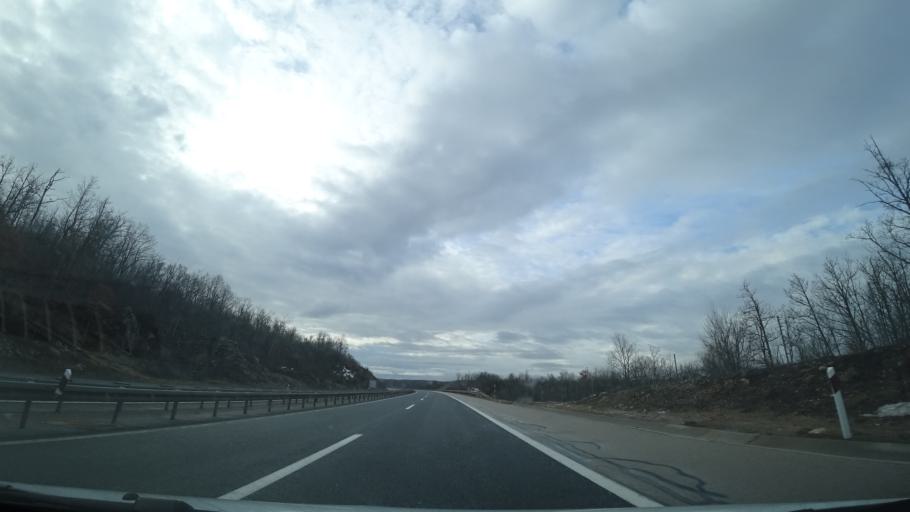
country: HR
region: Licko-Senjska
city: Otocac
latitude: 44.7410
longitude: 15.3784
